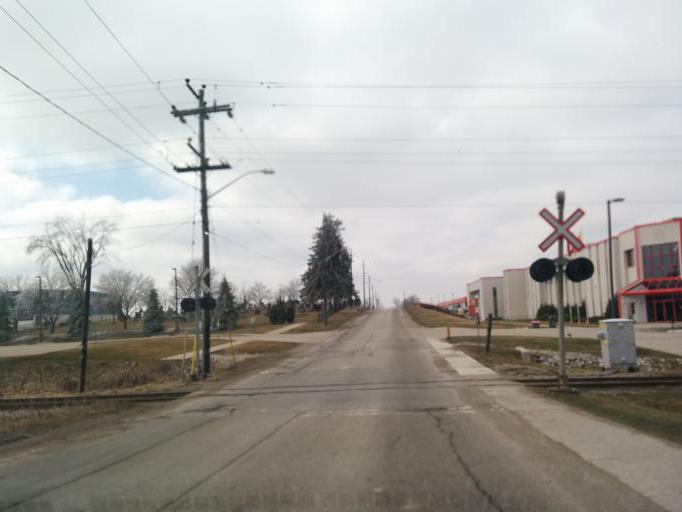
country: CA
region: Ontario
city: Waterloo
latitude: 43.5331
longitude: -80.5562
